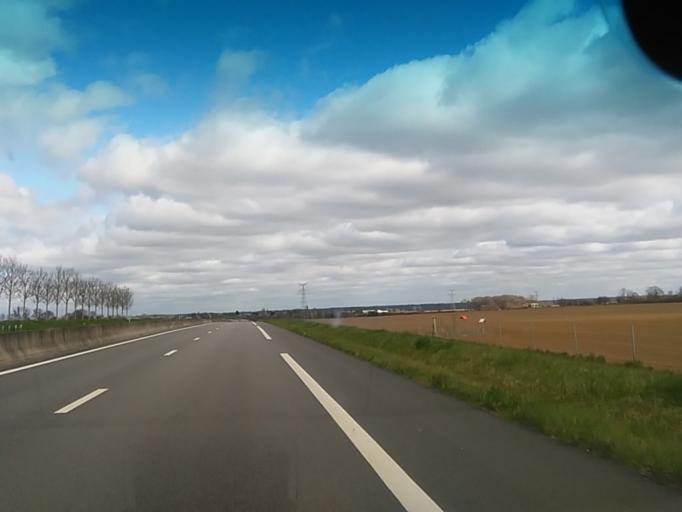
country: FR
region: Haute-Normandie
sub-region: Departement de l'Eure
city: Bourg-Achard
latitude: 49.3043
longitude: 0.8035
